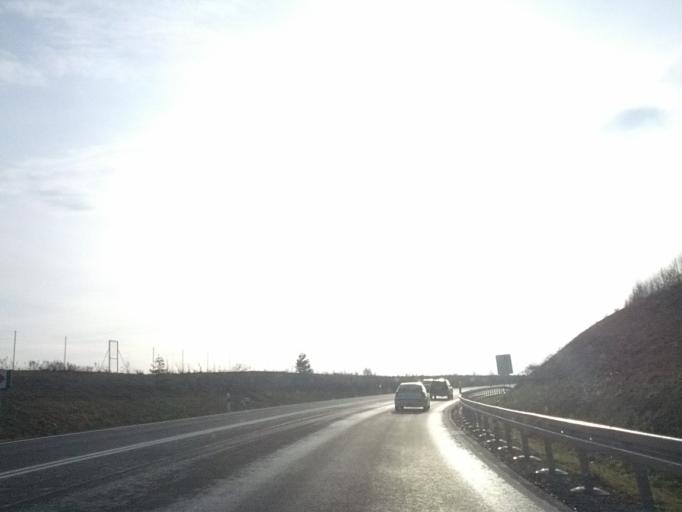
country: DE
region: Thuringia
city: Rohr
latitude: 50.5892
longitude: 10.4784
